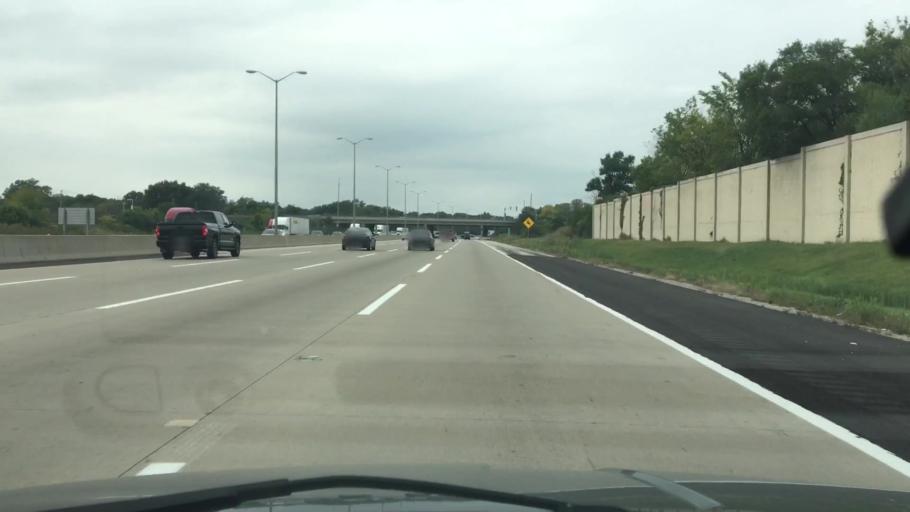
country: US
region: Illinois
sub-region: Cook County
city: Northbrook
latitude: 42.1155
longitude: -87.8744
